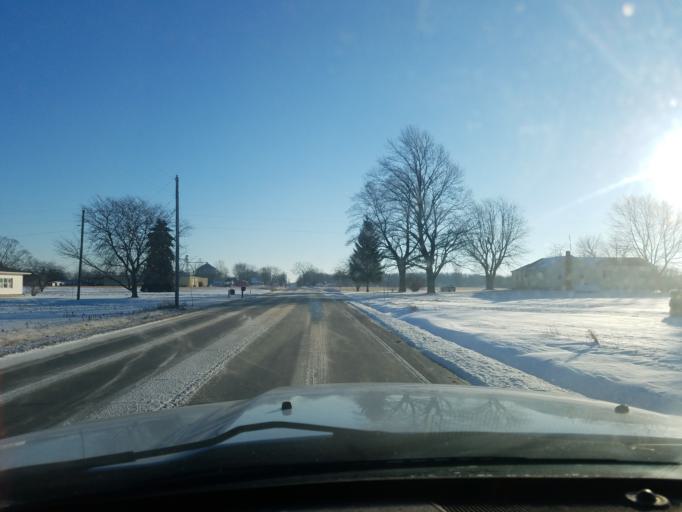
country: US
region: Indiana
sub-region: Noble County
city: Albion
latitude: 41.4570
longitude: -85.4913
